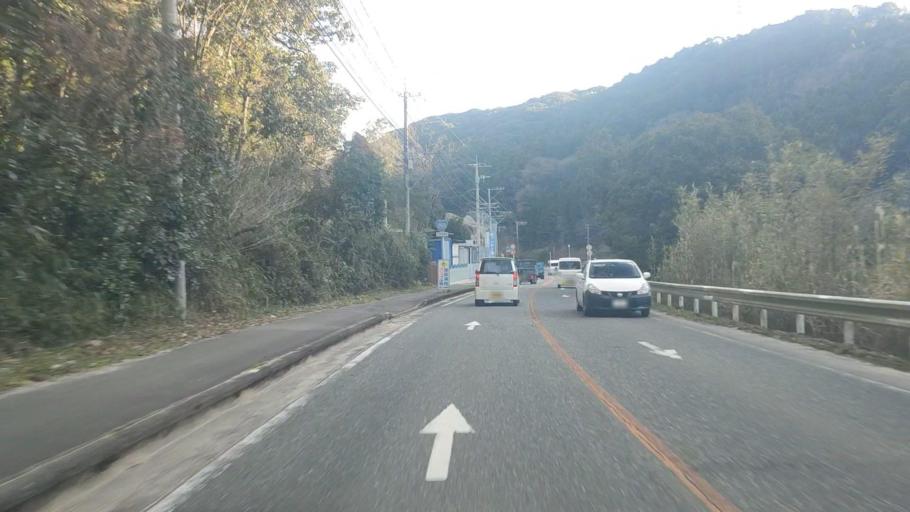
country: JP
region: Saga Prefecture
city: Saga-shi
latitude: 33.3342
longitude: 130.2625
